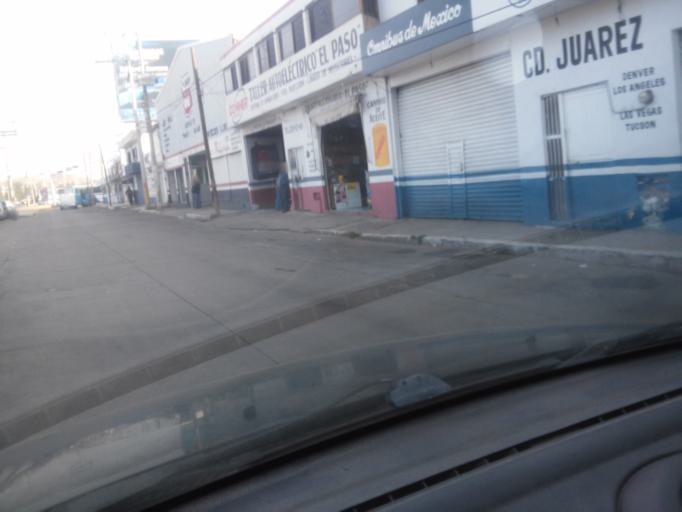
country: MX
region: Durango
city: Victoria de Durango
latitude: 24.0418
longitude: -104.6578
